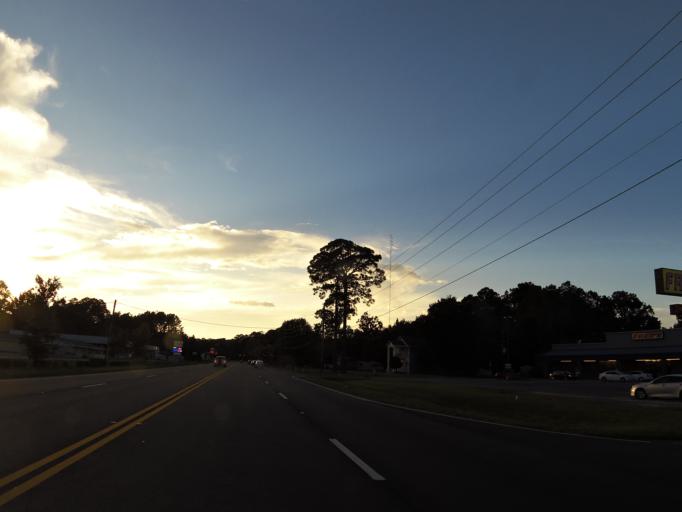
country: US
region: Georgia
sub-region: Camden County
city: Kingsland
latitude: 30.7987
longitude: -81.6767
